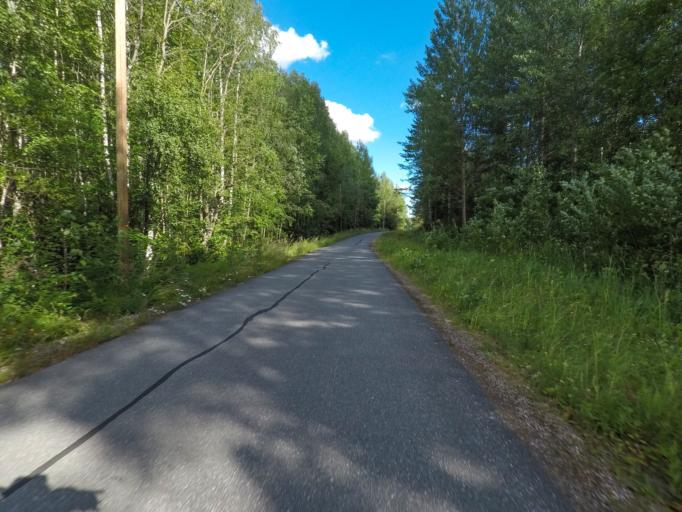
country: FI
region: South Karelia
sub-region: Lappeenranta
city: Lappeenranta
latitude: 61.1020
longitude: 28.1266
